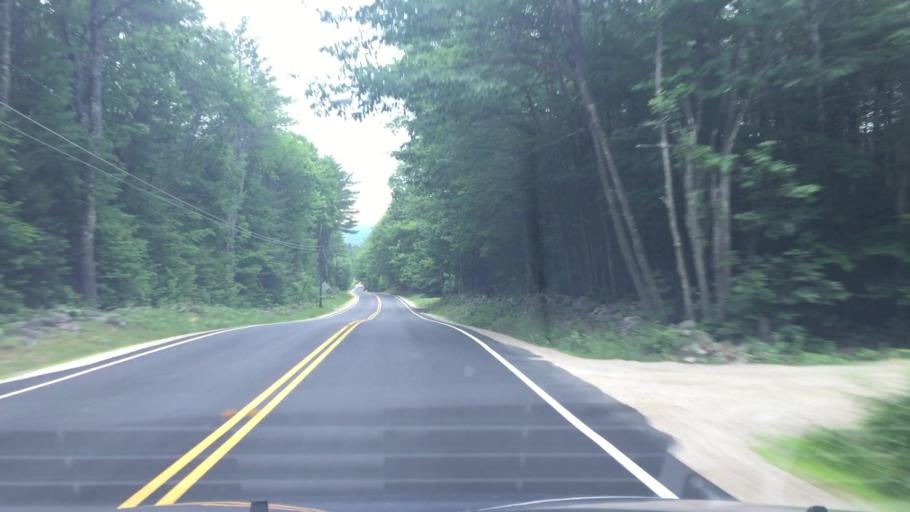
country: US
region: New Hampshire
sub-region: Carroll County
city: Freedom
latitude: 43.8357
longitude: -71.0782
